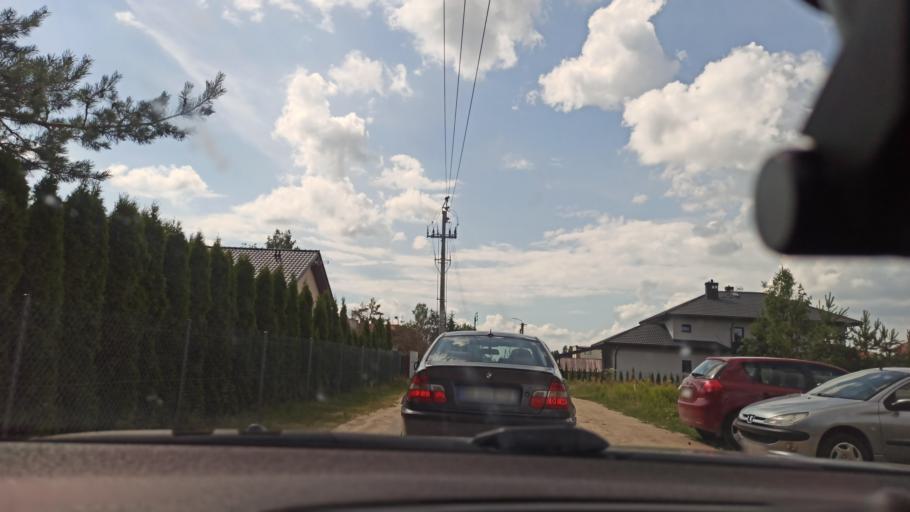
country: PL
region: Podlasie
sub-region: Powiat bialostocki
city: Turosn Koscielna
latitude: 53.0682
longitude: 23.1040
